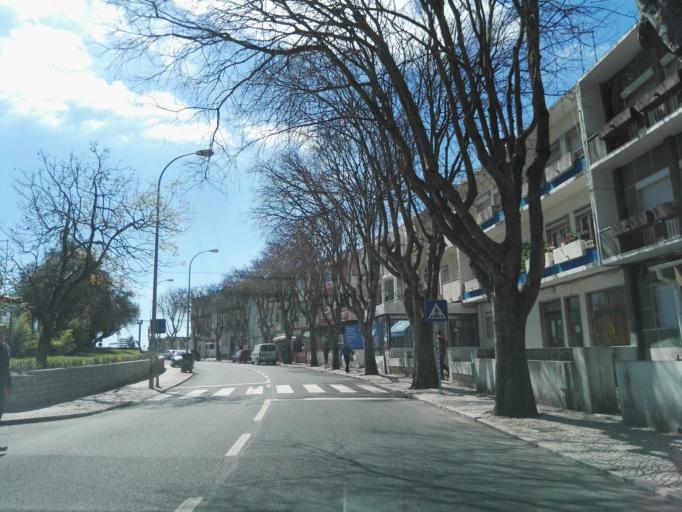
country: PT
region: Lisbon
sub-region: Oeiras
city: Barcarena
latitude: 38.7475
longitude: -9.2837
